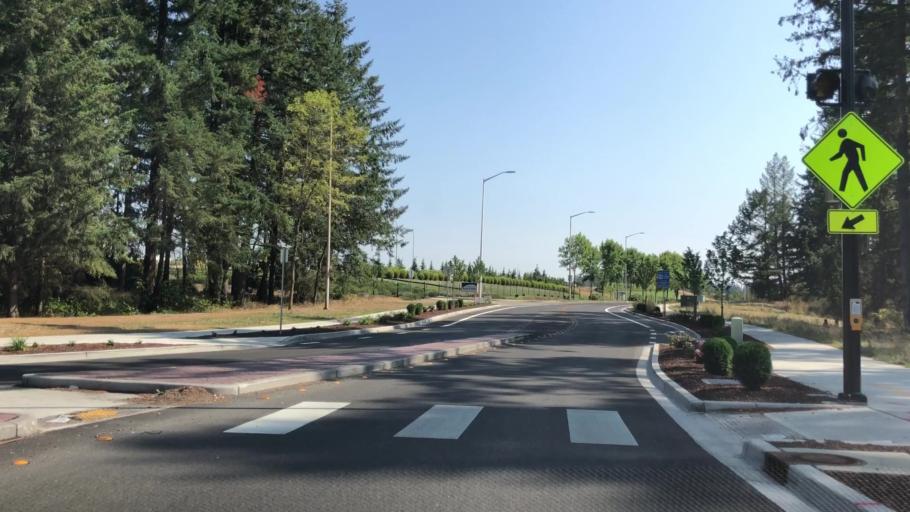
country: US
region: Washington
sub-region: Thurston County
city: Tanglewilde-Thompson Place
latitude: 47.0692
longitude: -122.7651
